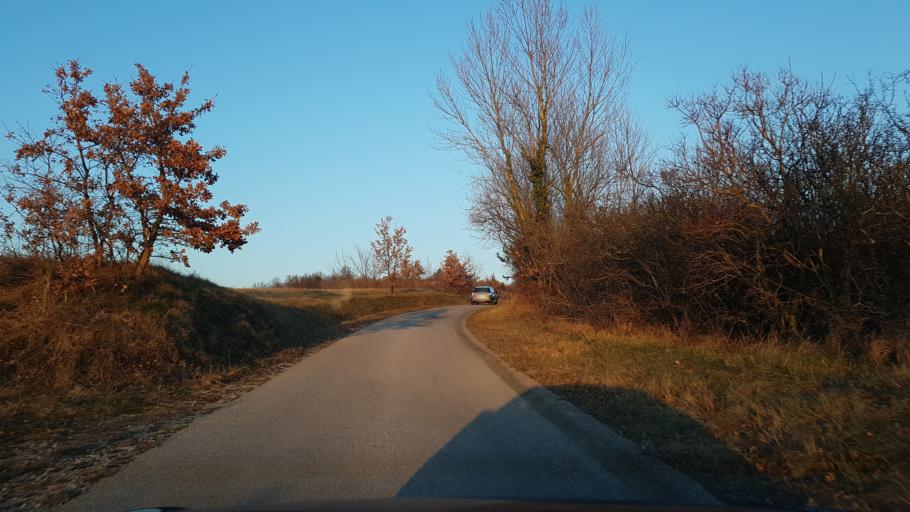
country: SI
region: Koper-Capodistria
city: Sv. Anton
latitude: 45.4922
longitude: 13.8427
